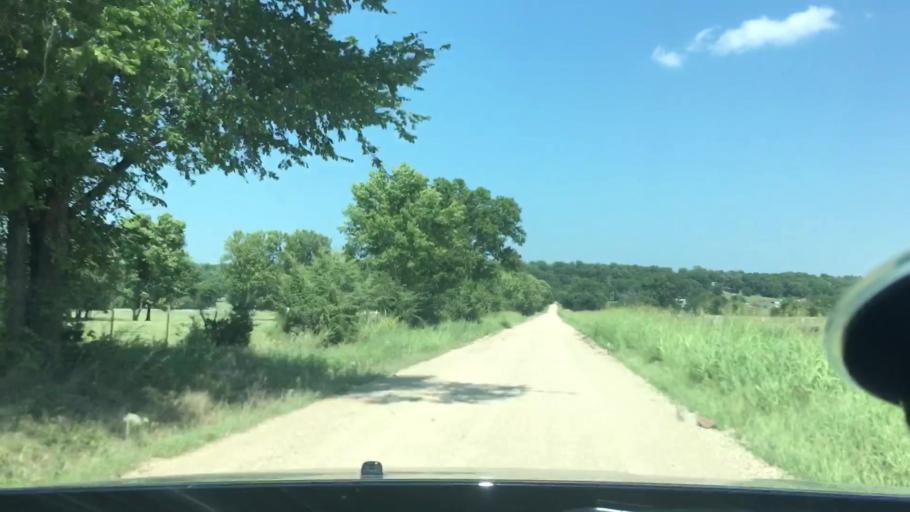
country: US
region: Oklahoma
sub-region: Johnston County
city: Tishomingo
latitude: 34.3569
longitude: -96.4420
